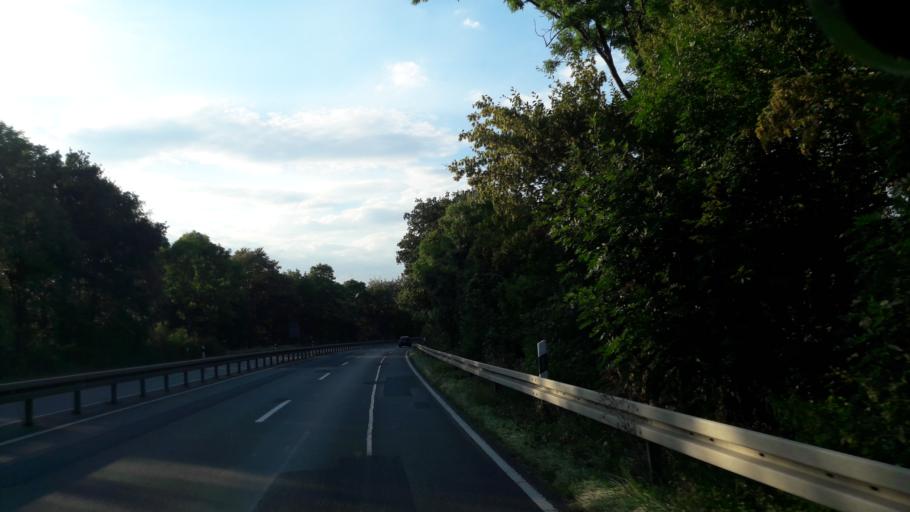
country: DE
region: Lower Saxony
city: Hildesheim
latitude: 52.1661
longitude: 9.9601
